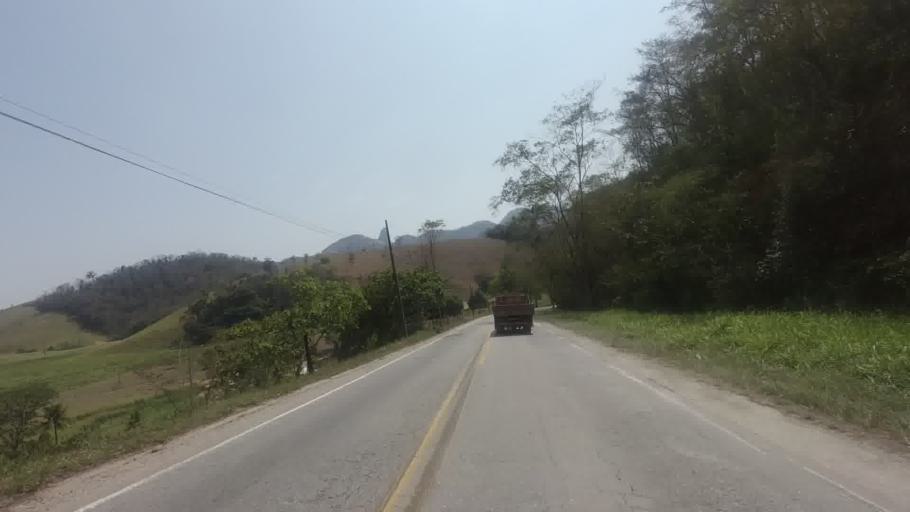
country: BR
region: Espirito Santo
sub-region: Cachoeiro De Itapemirim
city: Cachoeiro de Itapemirim
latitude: -20.8710
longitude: -41.0374
